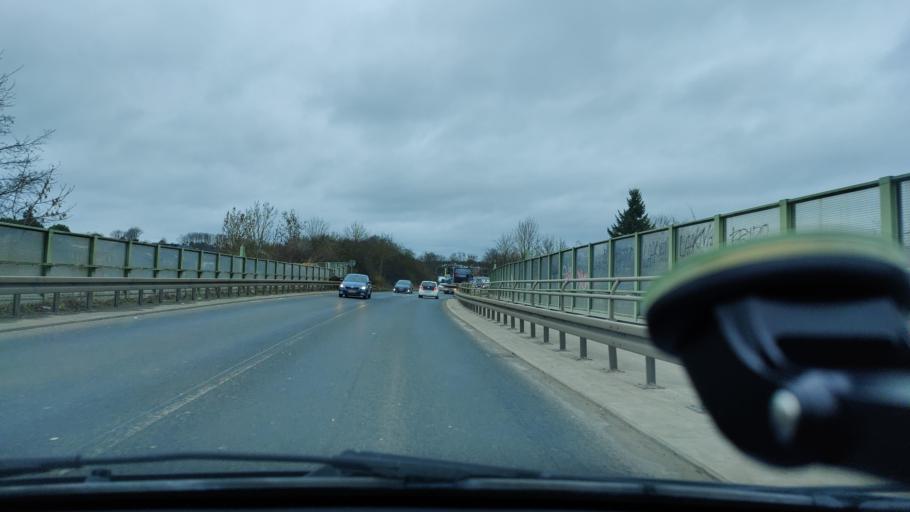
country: DE
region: North Rhine-Westphalia
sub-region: Regierungsbezirk Koln
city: Eschweiler
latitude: 50.8204
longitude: 6.2466
